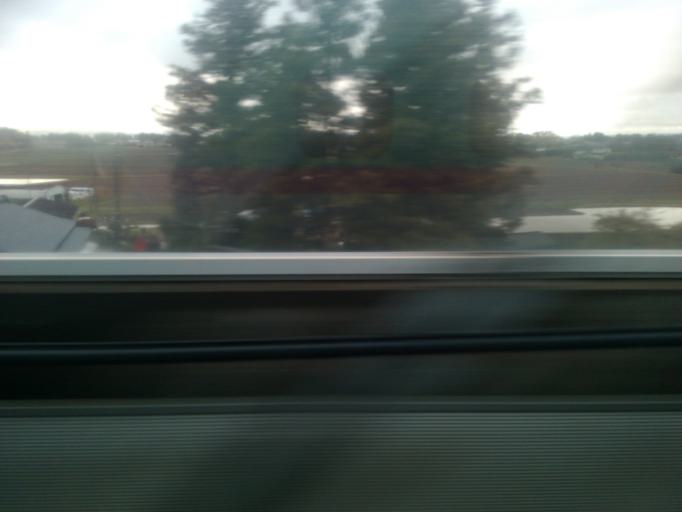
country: JP
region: Miyagi
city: Furukawa
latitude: 38.5967
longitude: 140.9800
